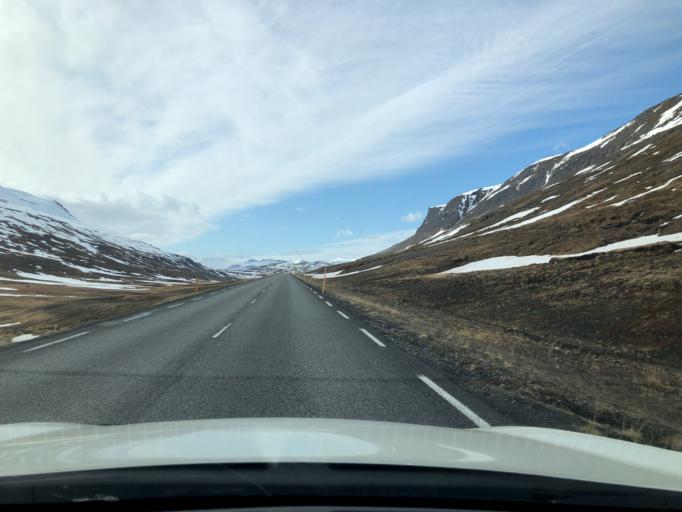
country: IS
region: East
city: Reydarfjoerdur
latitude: 65.1261
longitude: -14.3341
